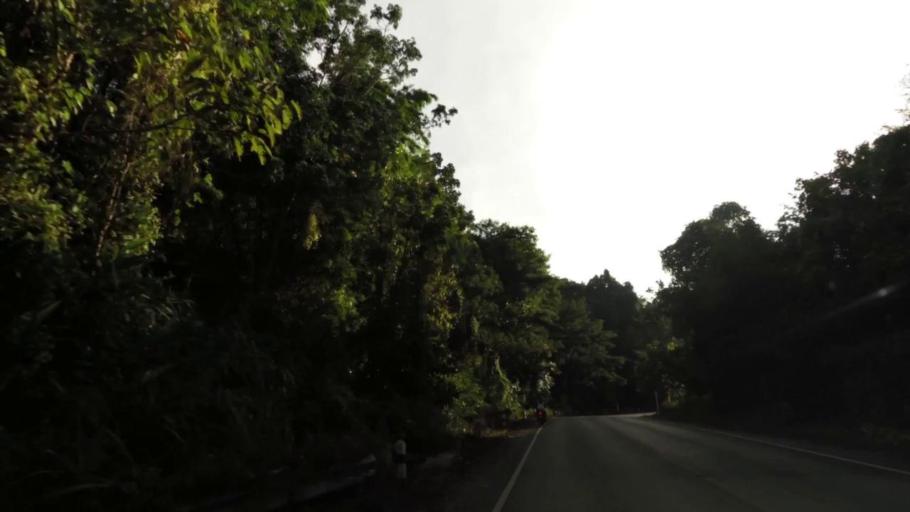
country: TH
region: Chiang Rai
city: Khun Tan
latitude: 19.8613
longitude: 100.4314
